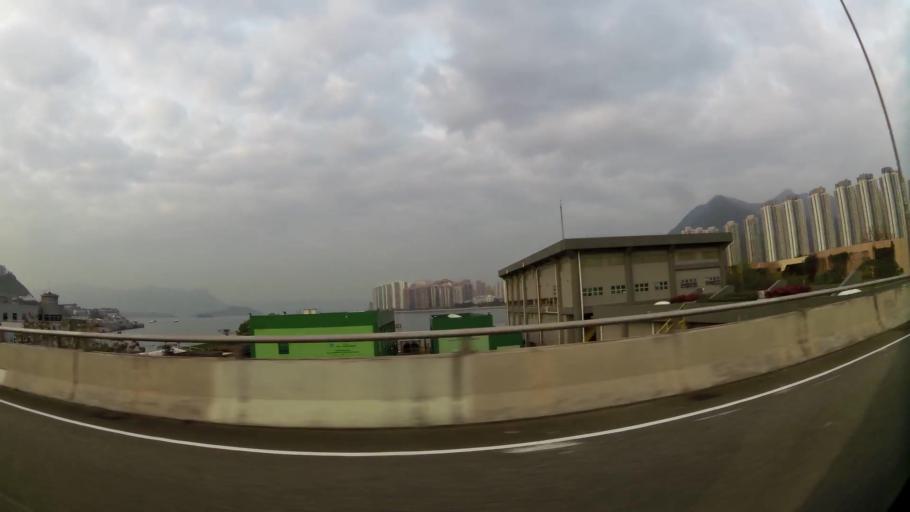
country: HK
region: Sha Tin
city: Sha Tin
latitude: 22.4093
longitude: 114.2146
